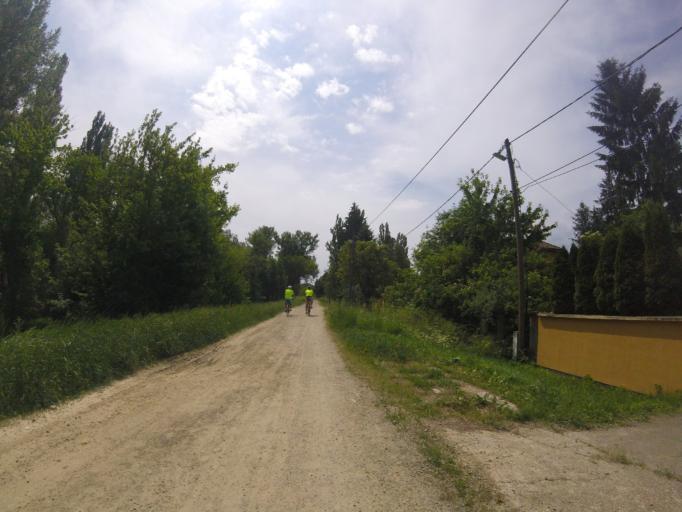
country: HU
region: Pest
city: God
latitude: 47.7131
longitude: 19.1211
